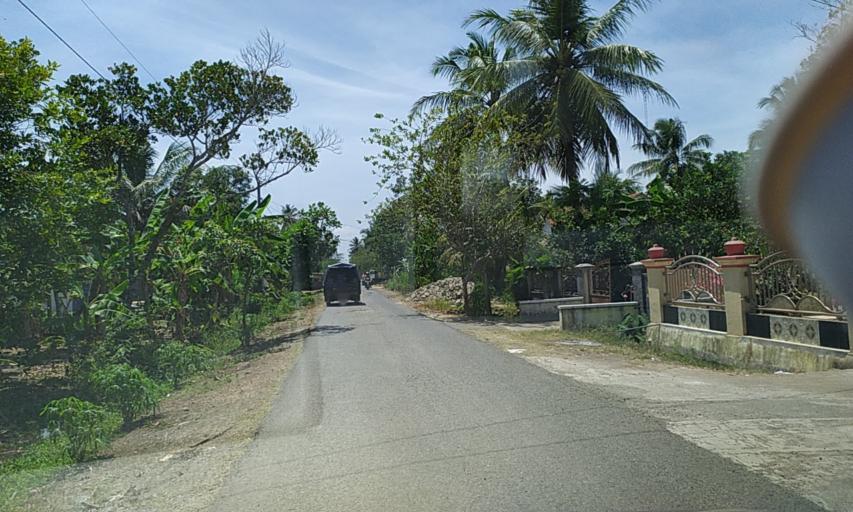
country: ID
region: Central Java
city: Cinyawang
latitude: -7.5590
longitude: 108.7565
